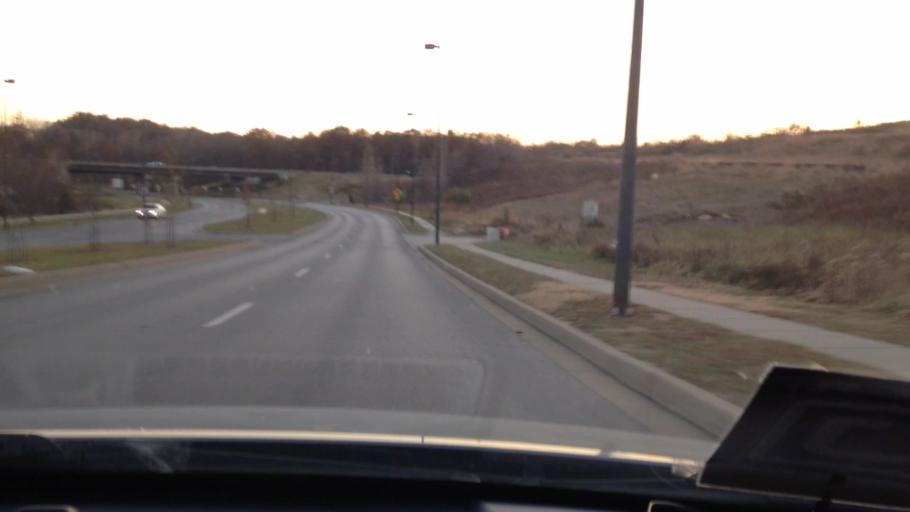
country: US
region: Missouri
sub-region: Clay County
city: Gladstone
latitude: 39.2608
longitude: -94.5573
